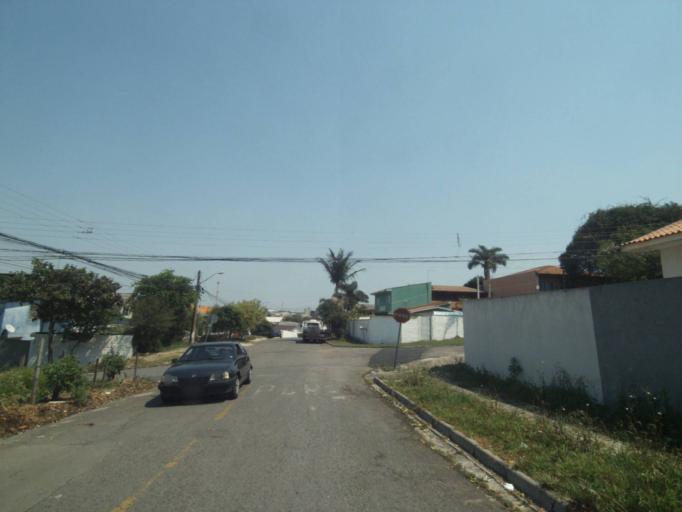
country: BR
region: Parana
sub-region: Sao Jose Dos Pinhais
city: Sao Jose dos Pinhais
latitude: -25.5089
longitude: -49.2748
